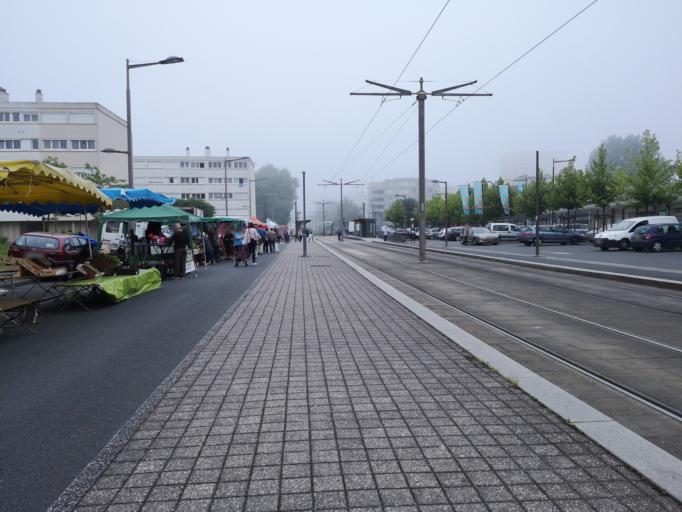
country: FR
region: Centre
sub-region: Departement du Loiret
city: Fleury-les-Aubrais
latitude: 47.9281
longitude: 1.9183
